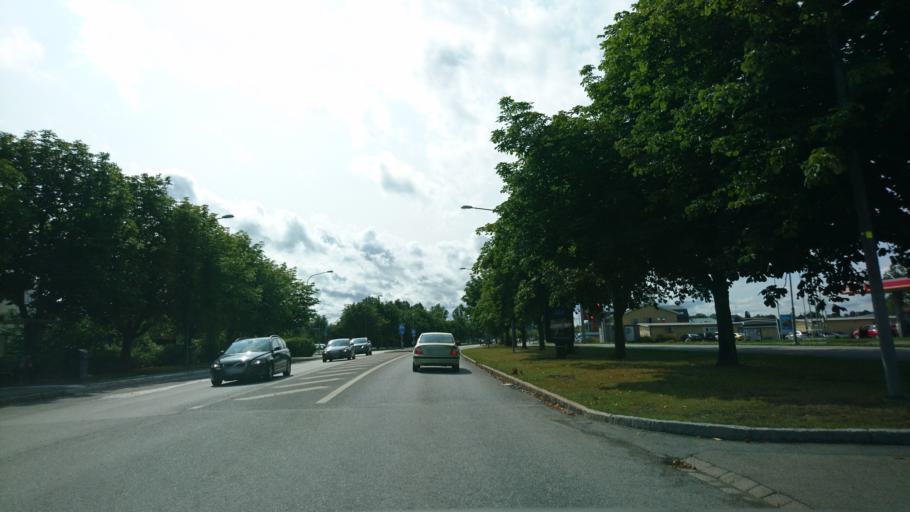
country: SE
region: Uppsala
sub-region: Uppsala Kommun
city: Uppsala
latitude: 59.8749
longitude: 17.6422
